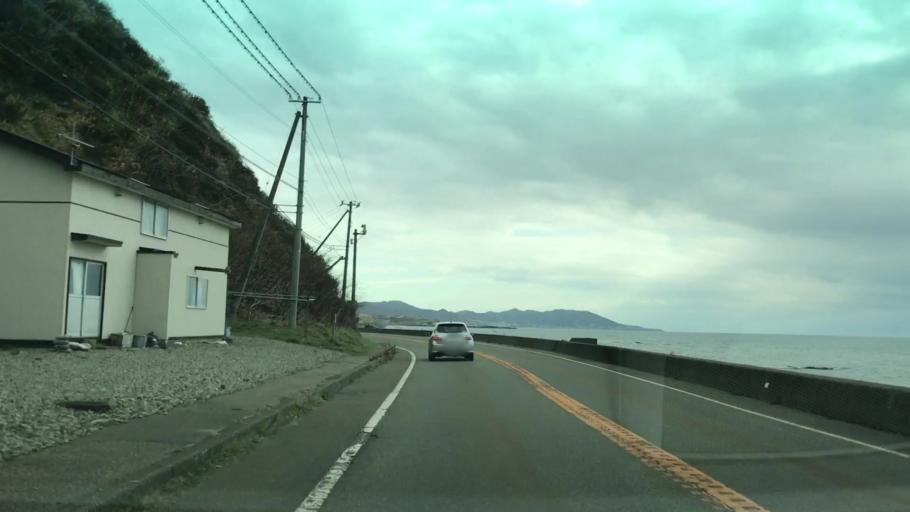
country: JP
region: Hokkaido
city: Shizunai-furukawacho
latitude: 42.0560
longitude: 143.0802
